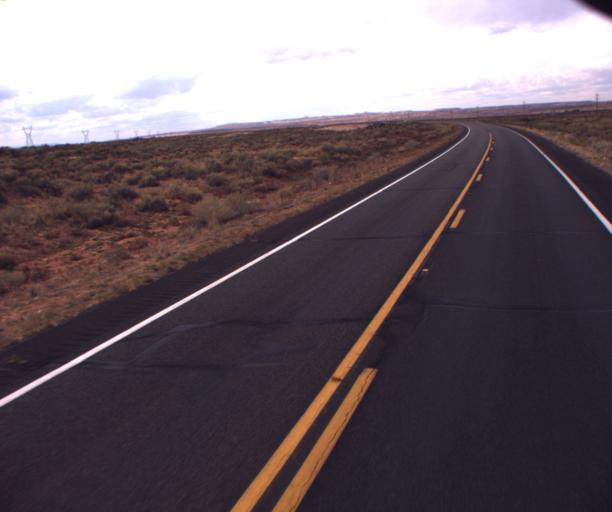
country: US
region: Arizona
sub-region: Apache County
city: Many Farms
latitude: 36.9410
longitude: -109.6449
